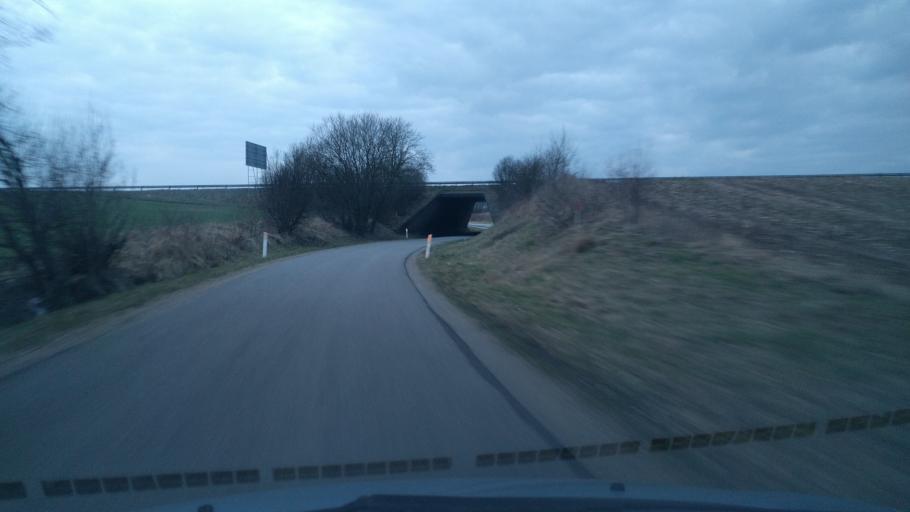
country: DK
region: South Denmark
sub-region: Haderslev Kommune
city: Haderslev
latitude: 55.2549
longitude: 9.4101
